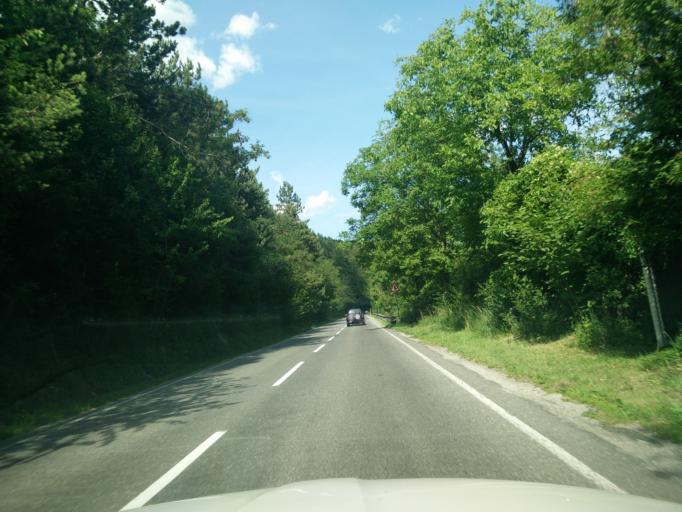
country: SK
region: Nitriansky
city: Prievidza
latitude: 48.8880
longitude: 18.6699
